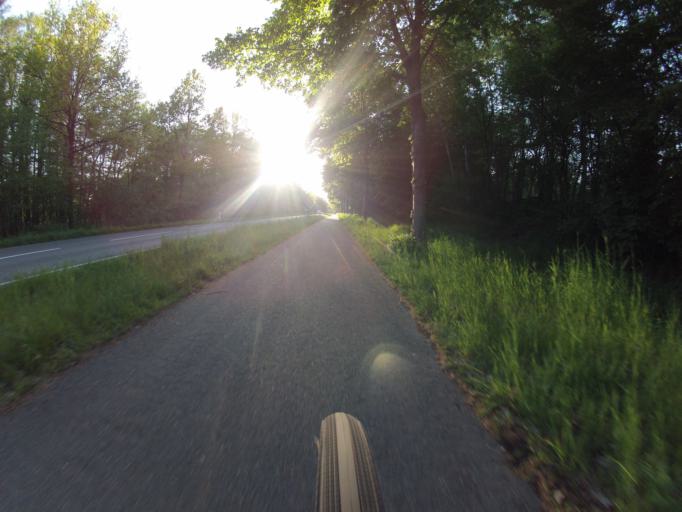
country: DE
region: North Rhine-Westphalia
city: Ibbenburen
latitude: 52.2625
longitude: 7.7530
